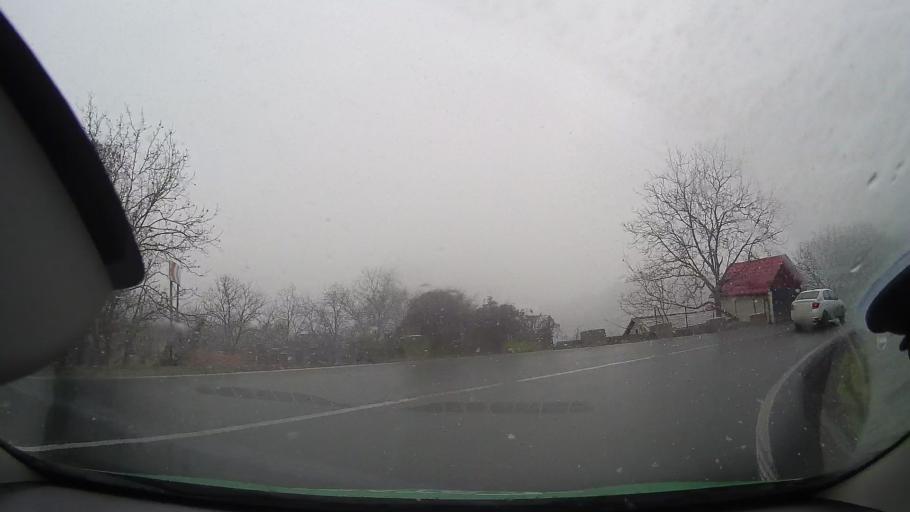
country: RO
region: Sibiu
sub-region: Municipiul Medias
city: Medias
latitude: 46.1791
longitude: 24.3411
